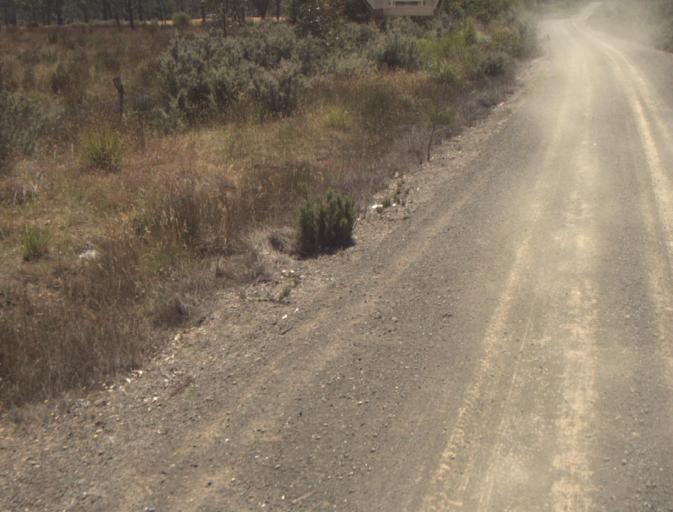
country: AU
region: Tasmania
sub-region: Launceston
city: Mayfield
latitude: -41.2763
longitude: 147.0987
